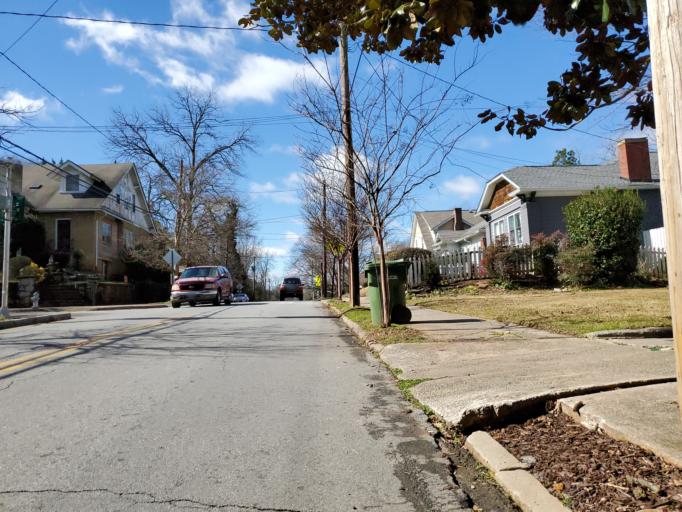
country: US
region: Georgia
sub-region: DeKalb County
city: Druid Hills
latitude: 33.7649
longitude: -84.3299
